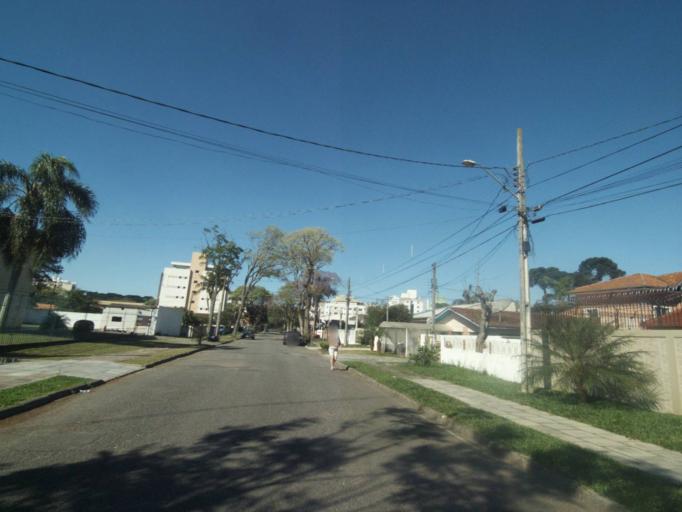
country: BR
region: Parana
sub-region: Curitiba
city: Curitiba
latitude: -25.3943
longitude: -49.2352
